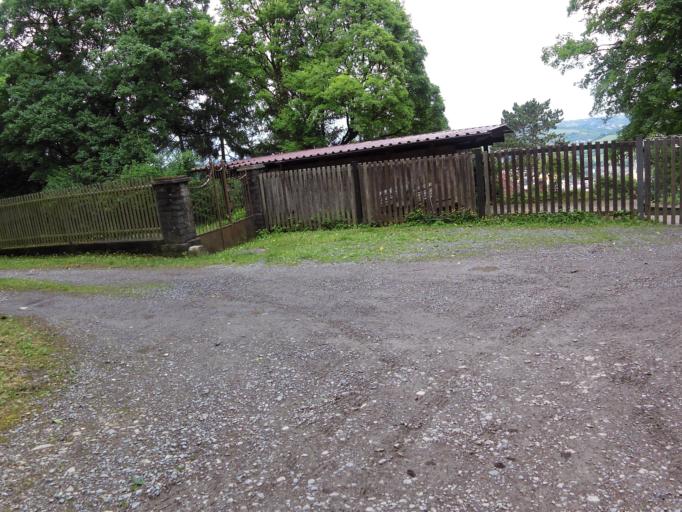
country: DE
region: Bavaria
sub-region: Regierungsbezirk Unterfranken
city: Hochberg
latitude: 49.7944
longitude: 9.8826
